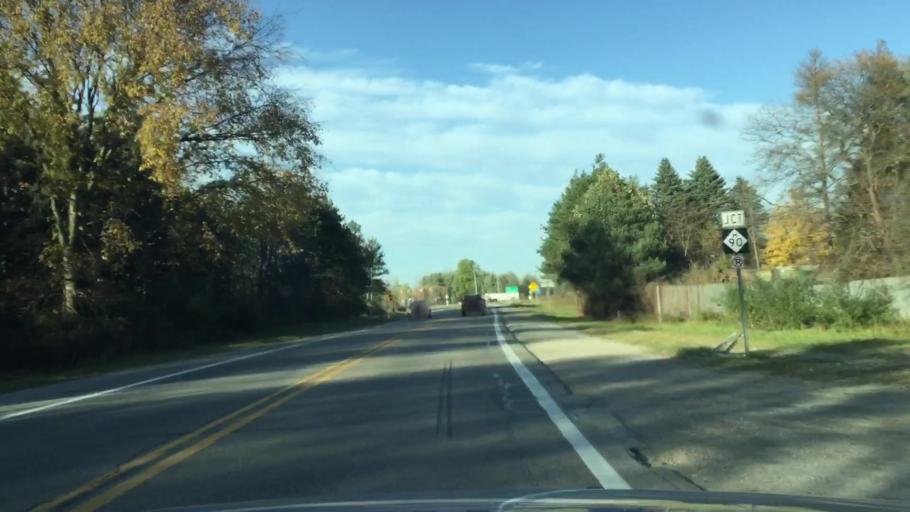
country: US
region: Michigan
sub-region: Lapeer County
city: Barnes Lake-Millers Lake
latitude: 43.2163
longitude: -83.3150
